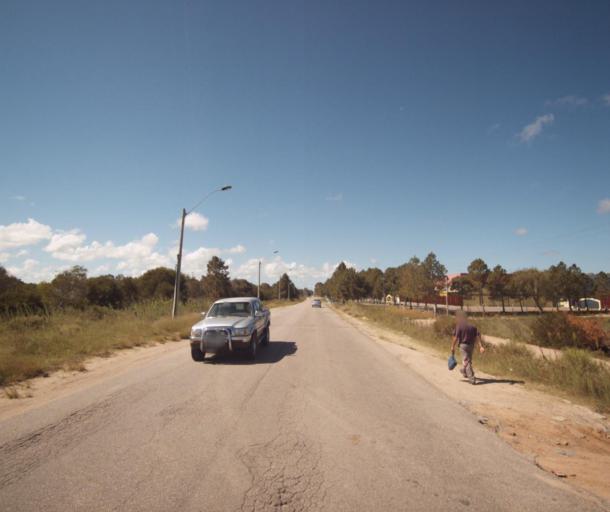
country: BR
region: Rio Grande do Sul
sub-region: Chui
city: Chui
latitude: -33.6849
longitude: -53.4520
